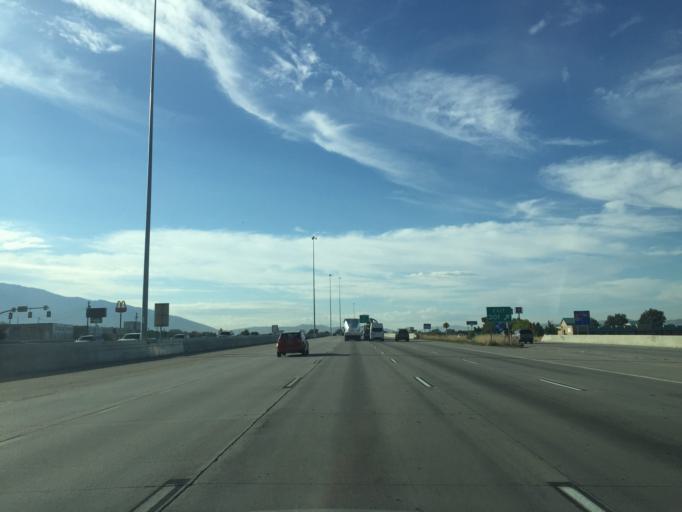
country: US
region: Utah
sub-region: Salt Lake County
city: Centerfield
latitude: 40.6784
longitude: -111.9021
